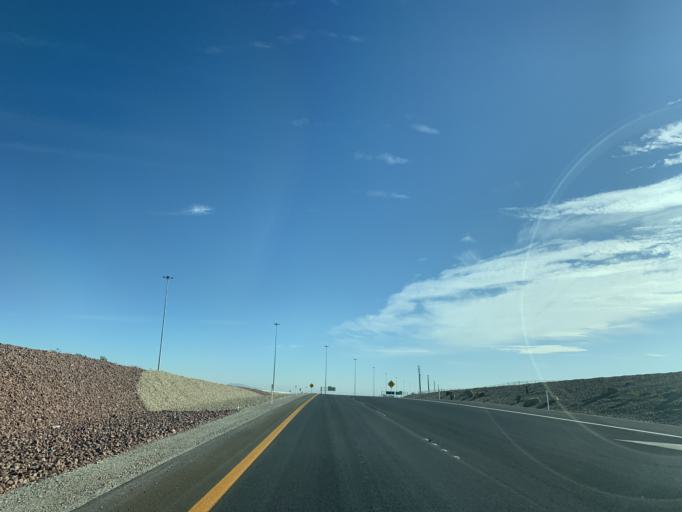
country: US
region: Nevada
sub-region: Clark County
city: Summerlin South
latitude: 36.3249
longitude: -115.3112
